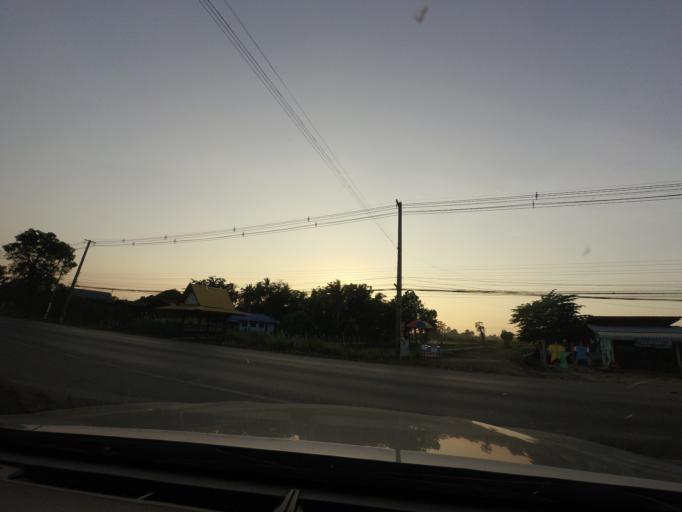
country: TH
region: Sukhothai
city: Si Samrong
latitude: 17.1306
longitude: 99.8504
